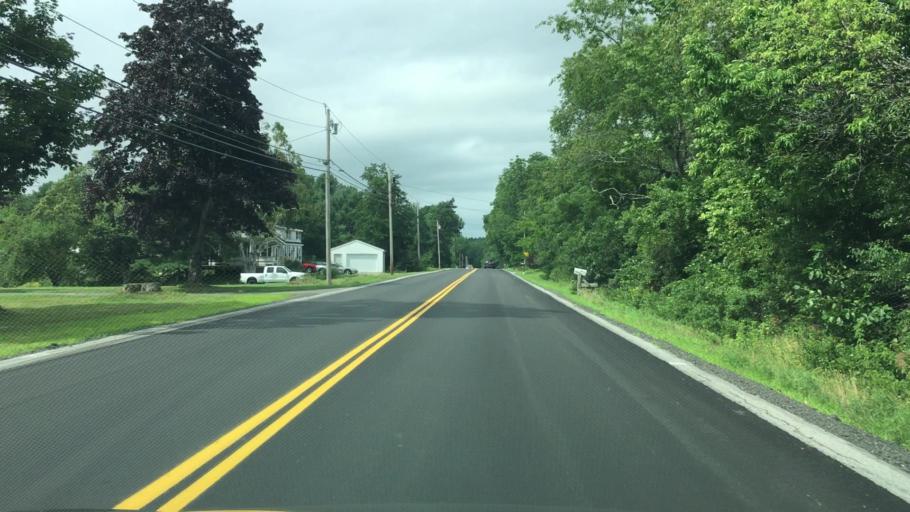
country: US
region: Maine
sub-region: Waldo County
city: Winterport
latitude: 44.6076
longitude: -68.8202
